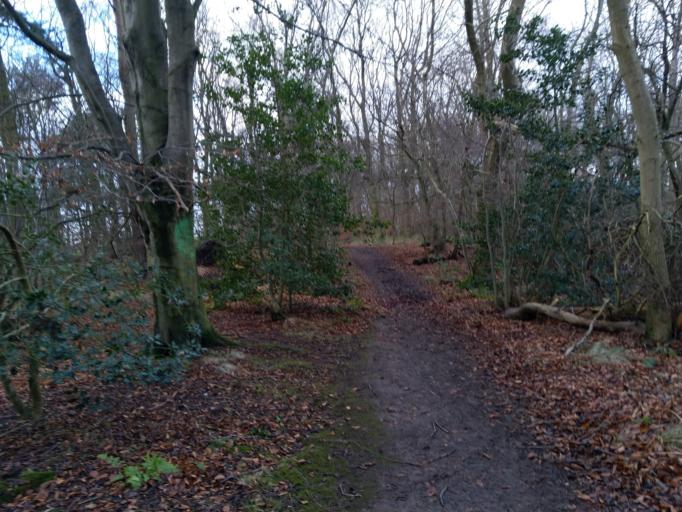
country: GB
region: Scotland
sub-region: Fife
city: Limekilns
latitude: 55.9993
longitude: -3.5153
